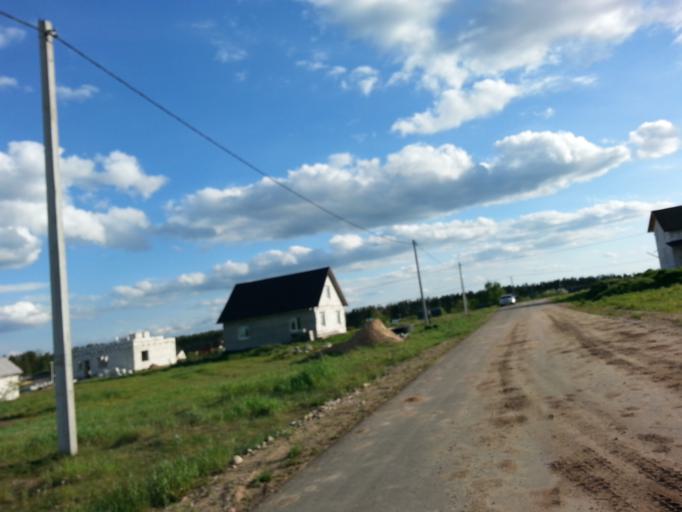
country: BY
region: Minsk
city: Narach
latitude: 54.9368
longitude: 26.7016
